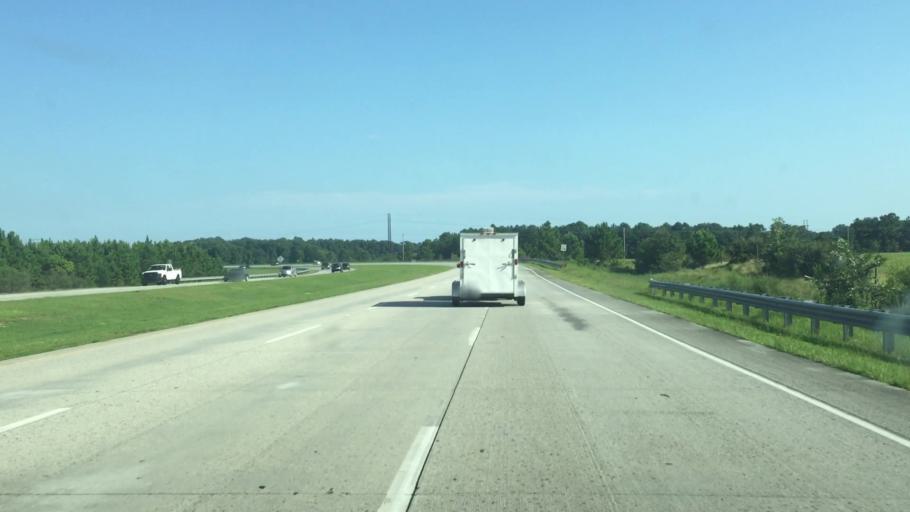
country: US
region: South Carolina
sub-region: Horry County
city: North Myrtle Beach
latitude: 33.8418
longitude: -78.7004
